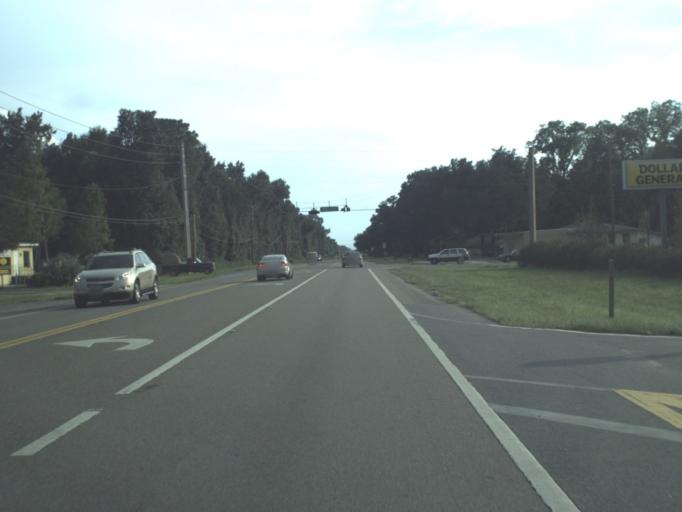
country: US
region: Florida
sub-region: Hernando County
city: Masaryktown
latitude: 28.4424
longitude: -82.4572
